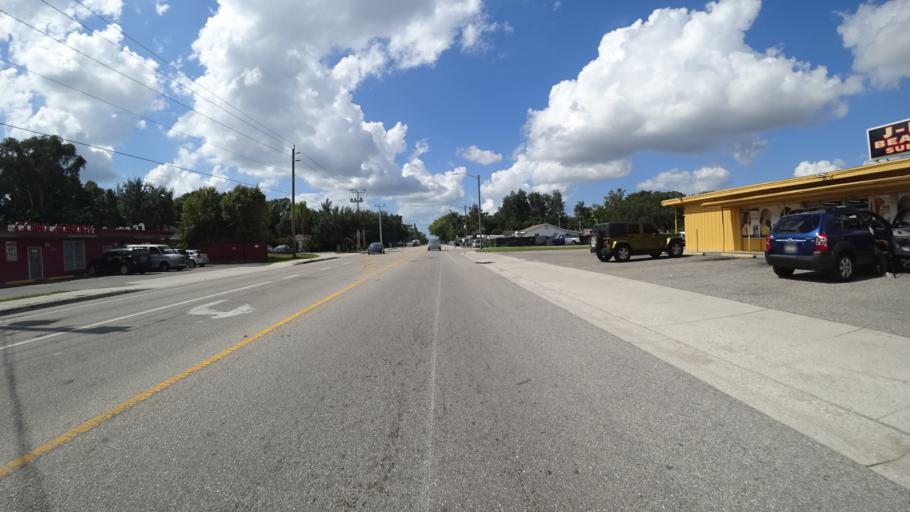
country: US
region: Florida
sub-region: Manatee County
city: Samoset
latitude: 27.4403
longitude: -82.5472
